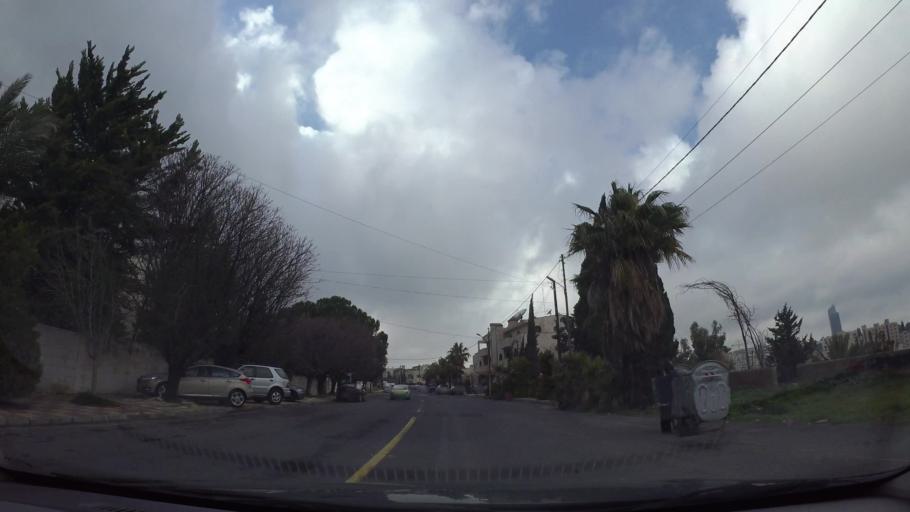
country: JO
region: Amman
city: Amman
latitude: 31.9476
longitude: 35.9007
